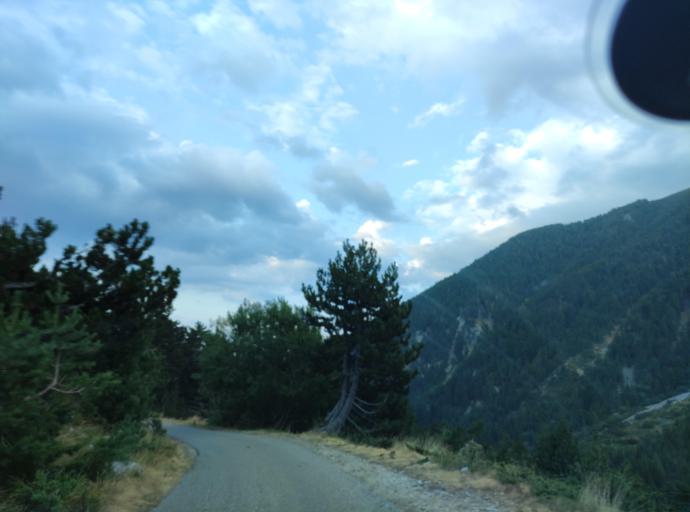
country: BG
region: Blagoevgrad
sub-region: Obshtina Bansko
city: Bansko
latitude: 41.7645
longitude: 23.4196
